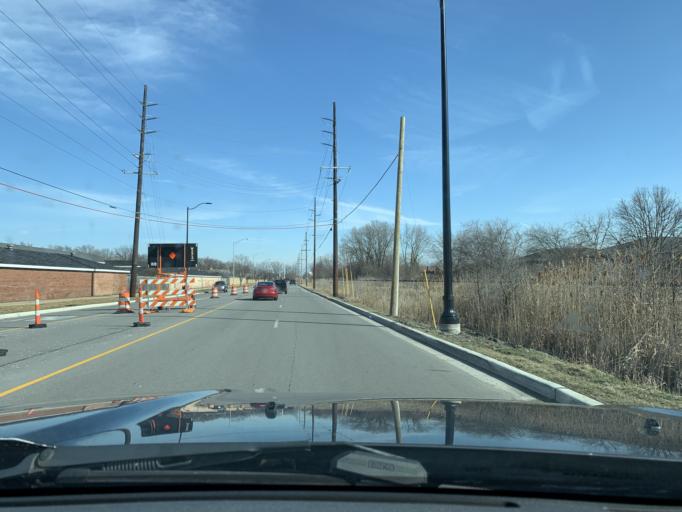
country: US
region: Indiana
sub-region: Lake County
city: Munster
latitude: 41.5392
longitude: -87.4997
